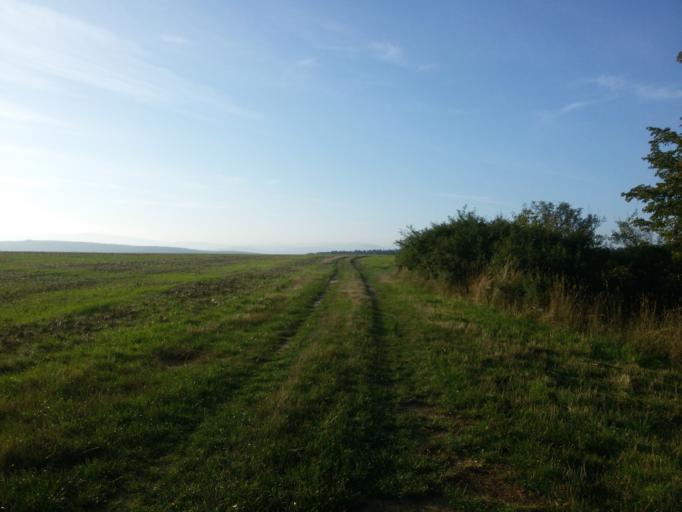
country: CZ
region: Zlin
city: Sumice
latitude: 49.0742
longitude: 17.6862
